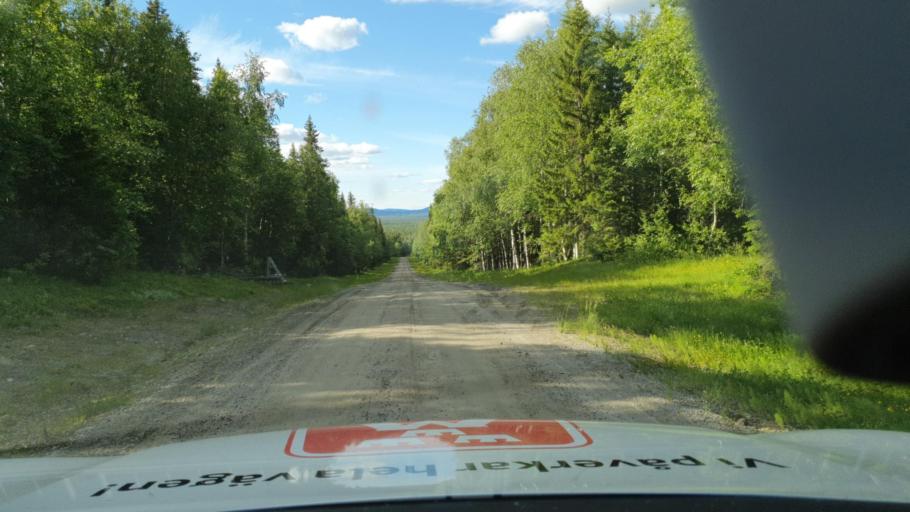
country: SE
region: Vaesterbotten
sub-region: Lycksele Kommun
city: Lycksele
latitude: 64.4236
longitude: 18.2794
